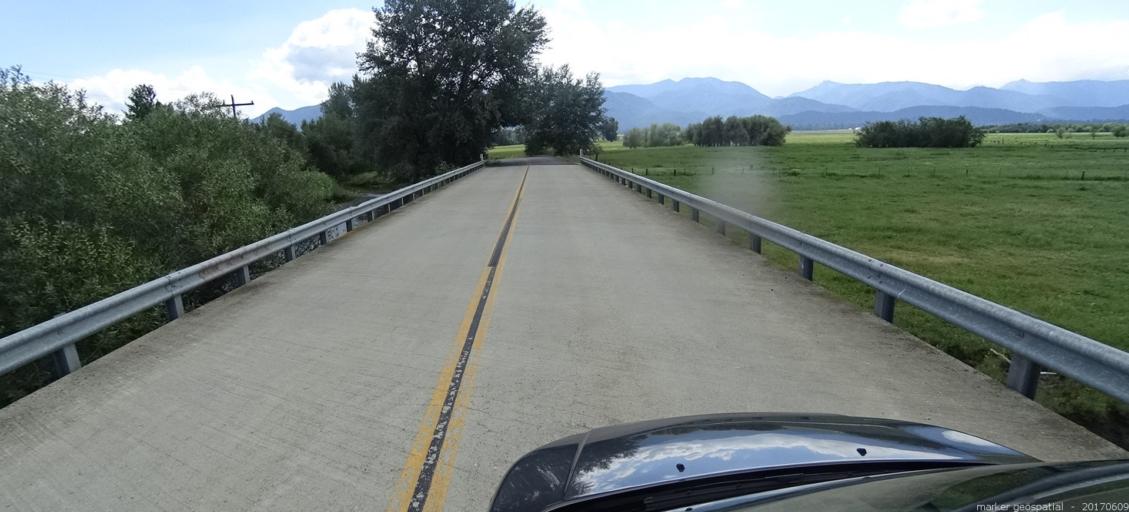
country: US
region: California
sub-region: Siskiyou County
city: Yreka
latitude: 41.5190
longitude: -122.8620
